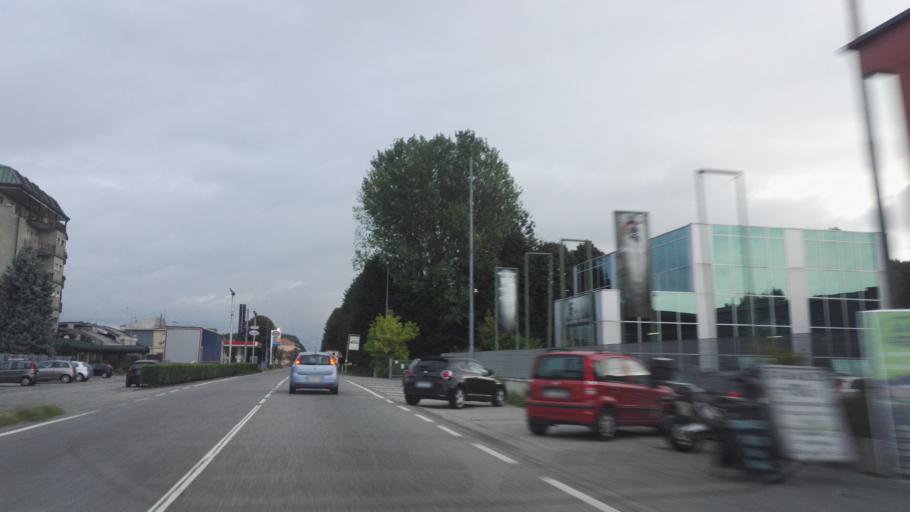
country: IT
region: Lombardy
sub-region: Citta metropolitana di Milano
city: Caleppio
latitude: 45.4326
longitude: 9.3782
